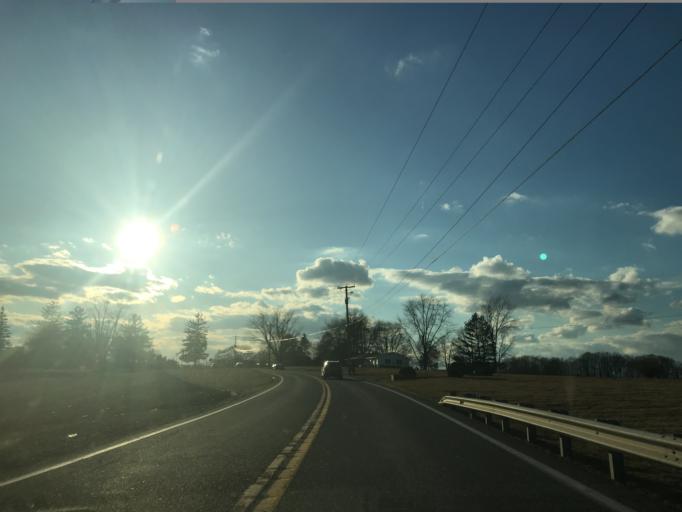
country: US
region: Pennsylvania
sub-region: York County
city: Susquehanna Trails
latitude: 39.7170
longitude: -76.3583
